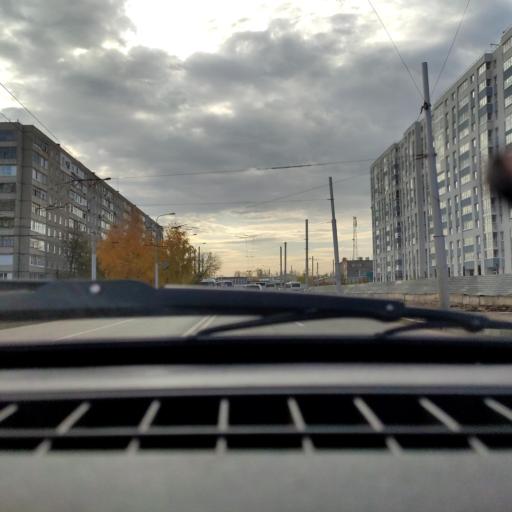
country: RU
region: Bashkortostan
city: Ufa
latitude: 54.7766
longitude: 56.1243
